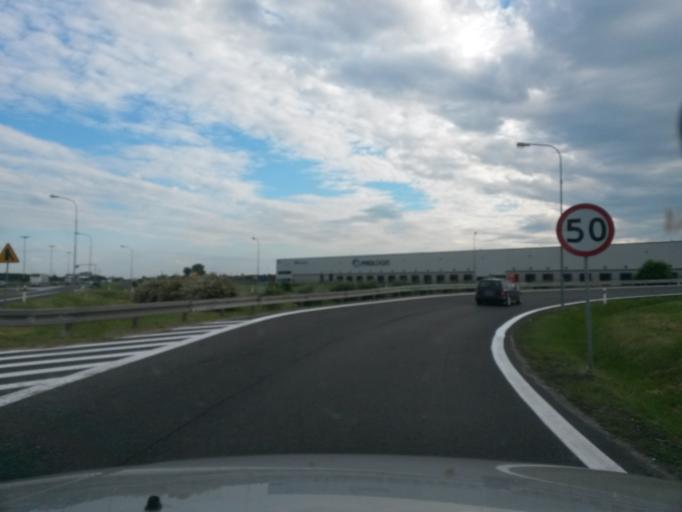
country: PL
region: Lodz Voivodeship
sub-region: Piotrkow Trybunalski
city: Piotrkow Trybunalski
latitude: 51.4094
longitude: 19.6340
